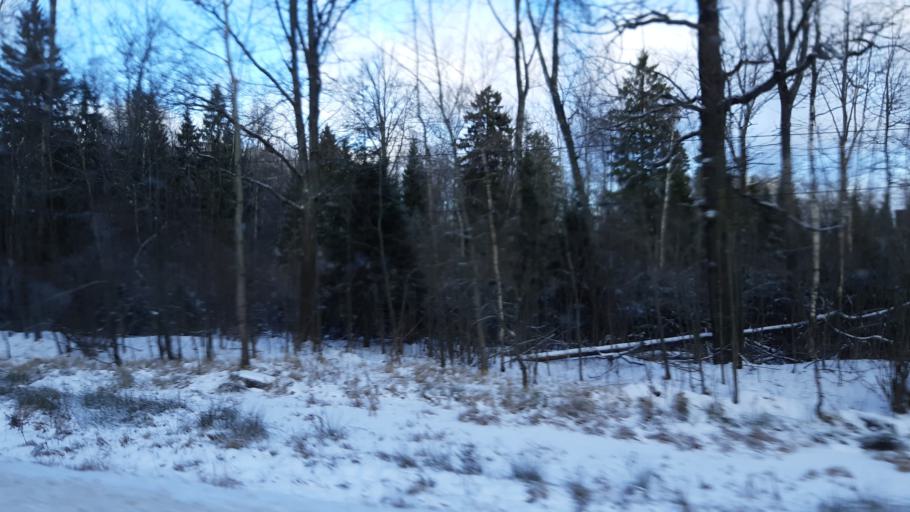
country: RU
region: Moskovskaya
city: Svatkovo
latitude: 56.3161
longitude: 38.3049
